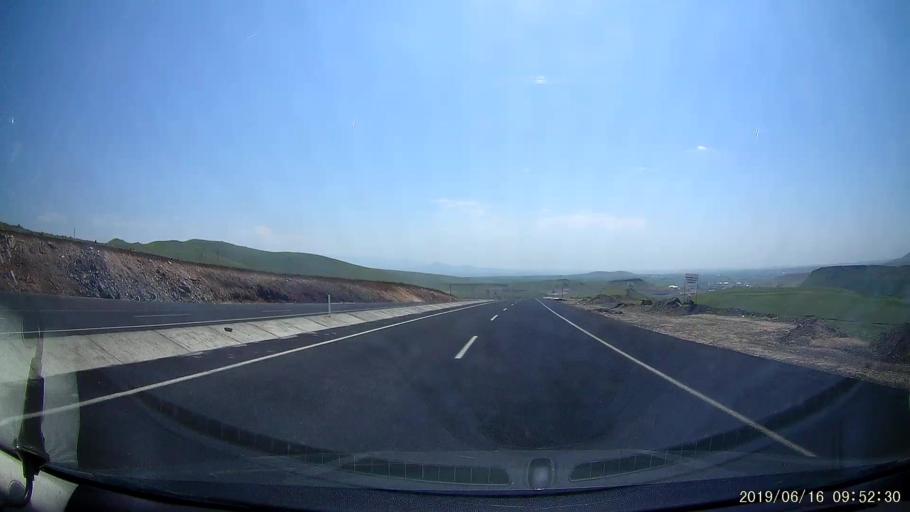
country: TR
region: Kars
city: Digor
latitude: 40.3941
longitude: 43.3883
